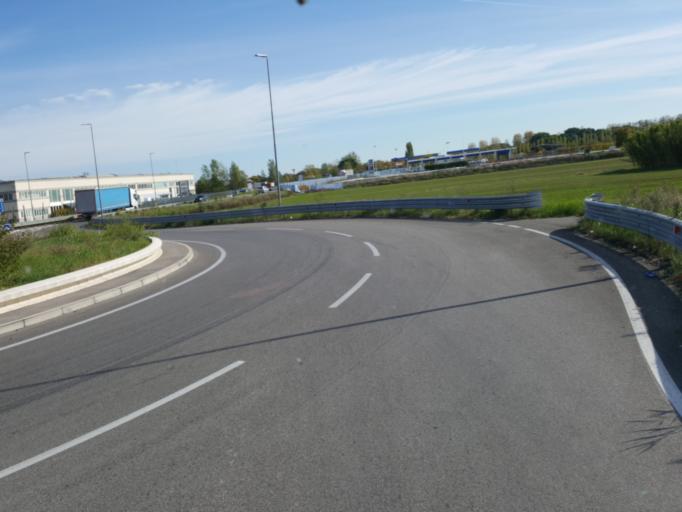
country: IT
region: Emilia-Romagna
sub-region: Forli-Cesena
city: Forli
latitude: 44.2167
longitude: 12.0786
